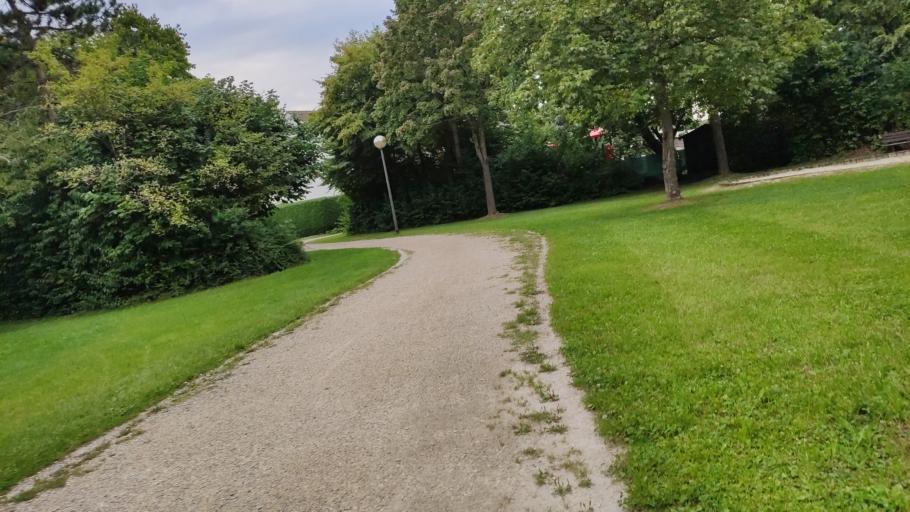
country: DE
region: Bavaria
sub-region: Swabia
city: Konigsbrunn
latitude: 48.2775
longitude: 10.8795
